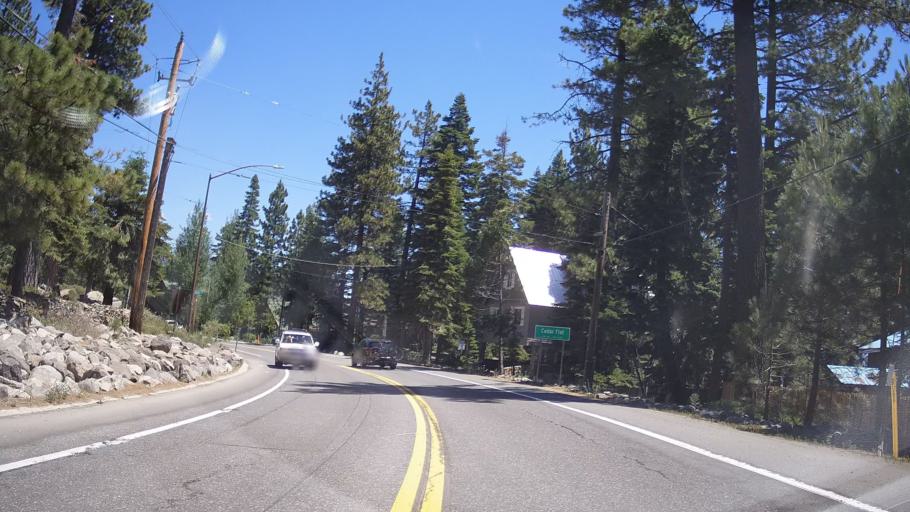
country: US
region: California
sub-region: Placer County
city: Dollar Point
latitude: 39.2088
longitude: -120.0906
